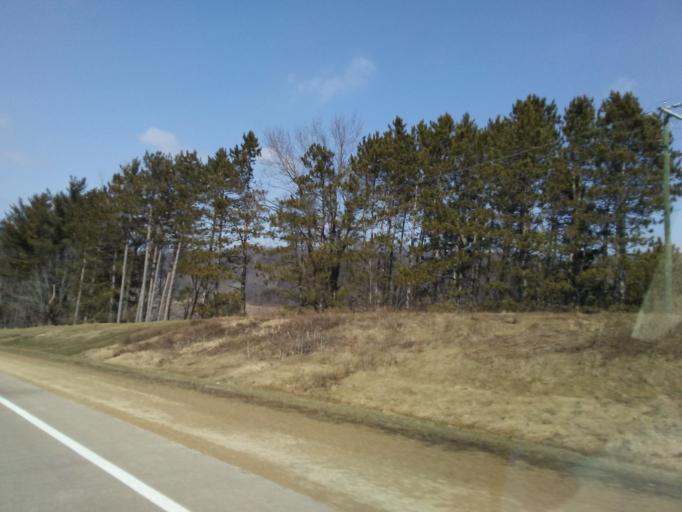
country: US
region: Wisconsin
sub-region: La Crosse County
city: La Crosse
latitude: 43.7504
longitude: -91.1140
